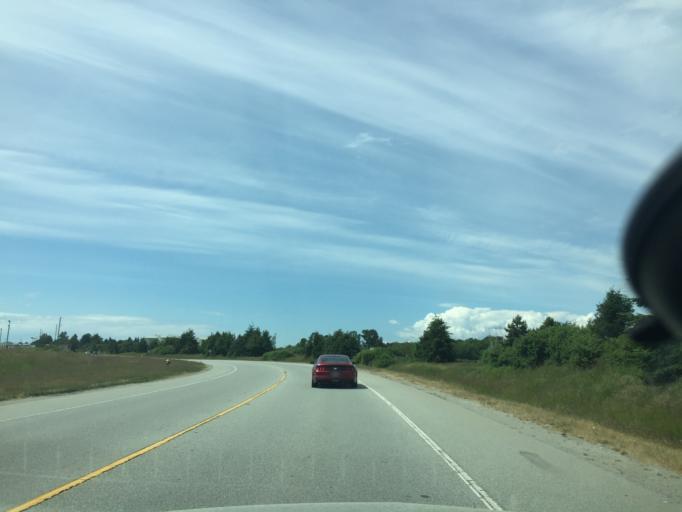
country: CA
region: British Columbia
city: Richmond
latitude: 49.2043
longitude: -123.1543
